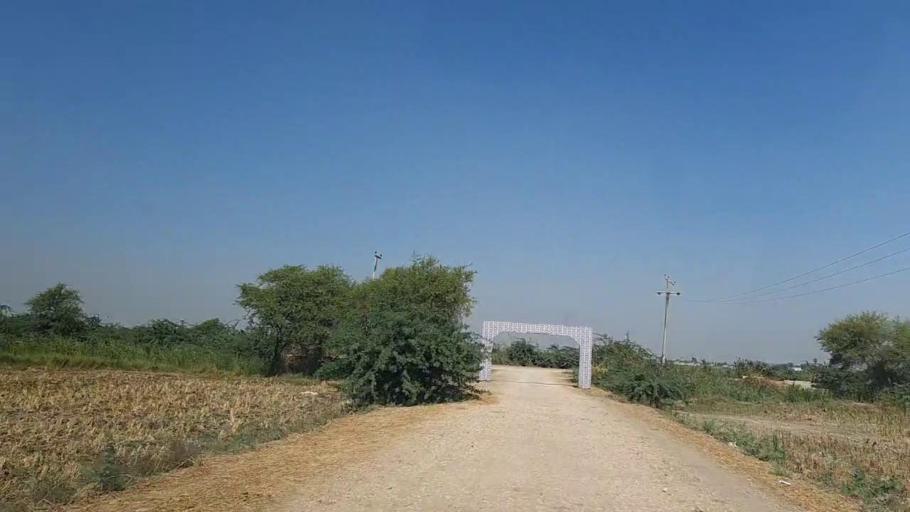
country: PK
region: Sindh
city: Daro Mehar
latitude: 24.7935
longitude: 68.1725
